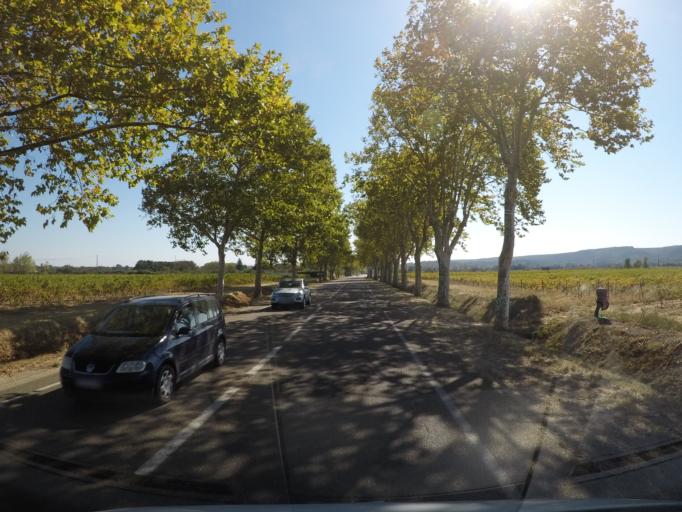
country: FR
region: Languedoc-Roussillon
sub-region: Departement du Gard
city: Castillon-du-Gard
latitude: 43.9681
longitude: 4.5053
